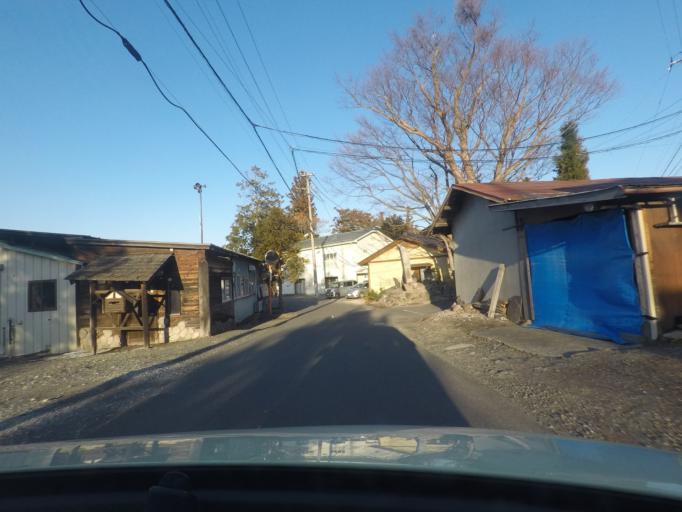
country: JP
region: Nagano
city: Matsumoto
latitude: 36.2154
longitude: 137.8924
